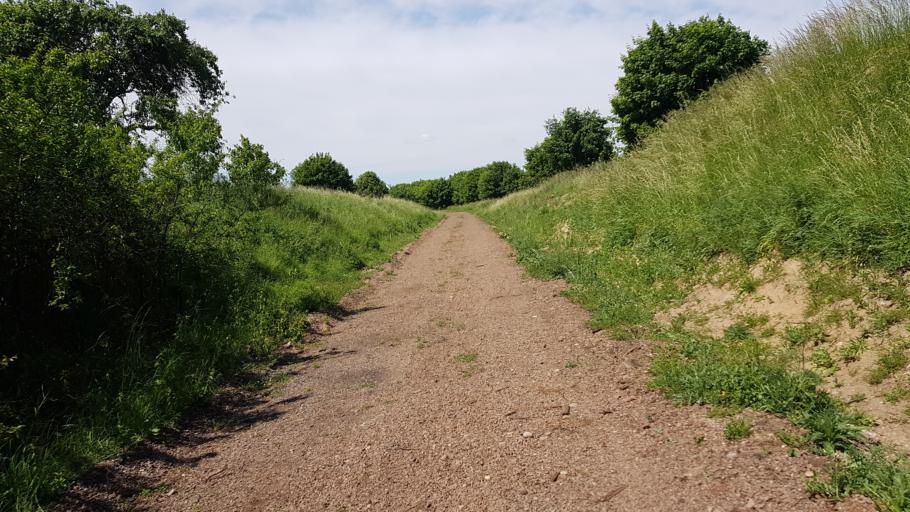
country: PL
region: West Pomeranian Voivodeship
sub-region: Powiat mysliborski
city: Barlinek
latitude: 52.9910
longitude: 15.1924
